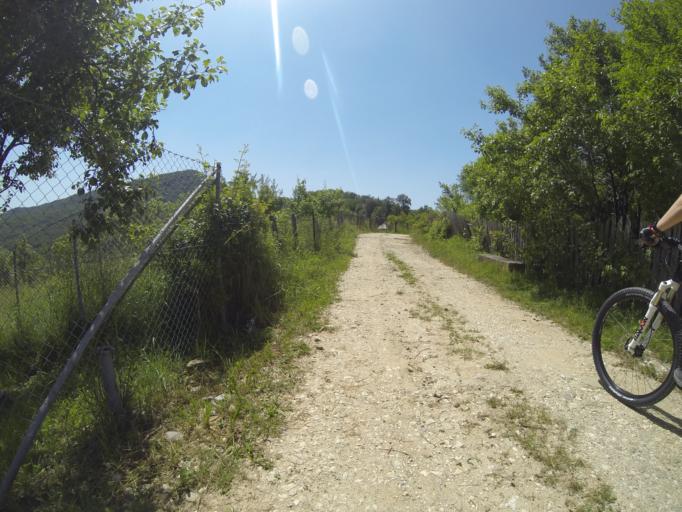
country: RO
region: Valcea
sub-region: Oras Baile Olanesti
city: Baile Olanesti
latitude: 45.2024
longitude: 24.2140
